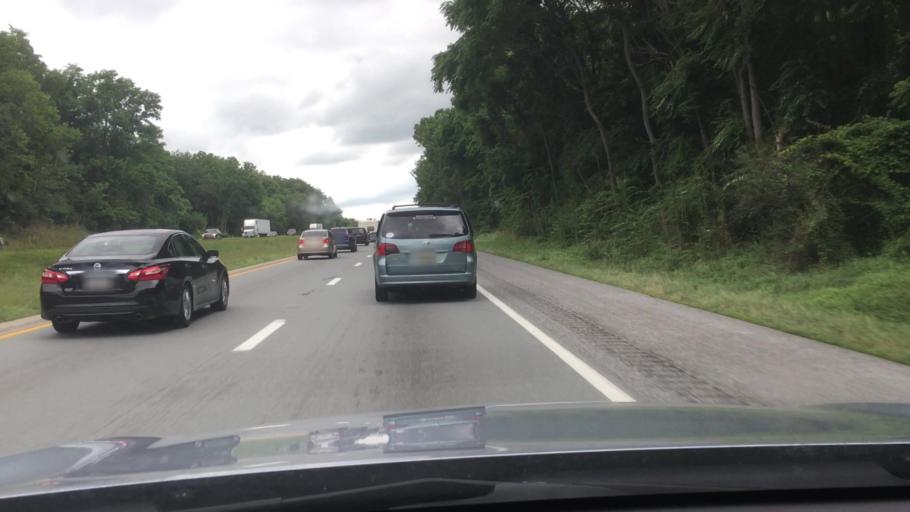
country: US
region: Pennsylvania
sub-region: Cumberland County
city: Newville
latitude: 40.1517
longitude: -77.3068
